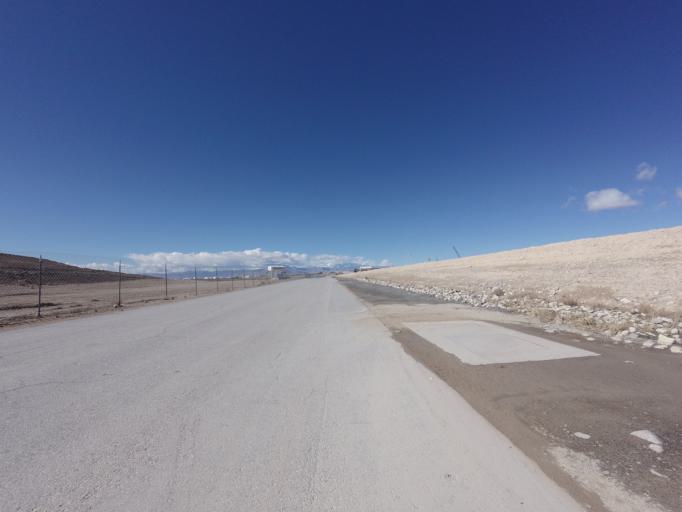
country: US
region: Nevada
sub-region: Clark County
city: Nellis Air Force Base
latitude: 36.2583
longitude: -115.0268
